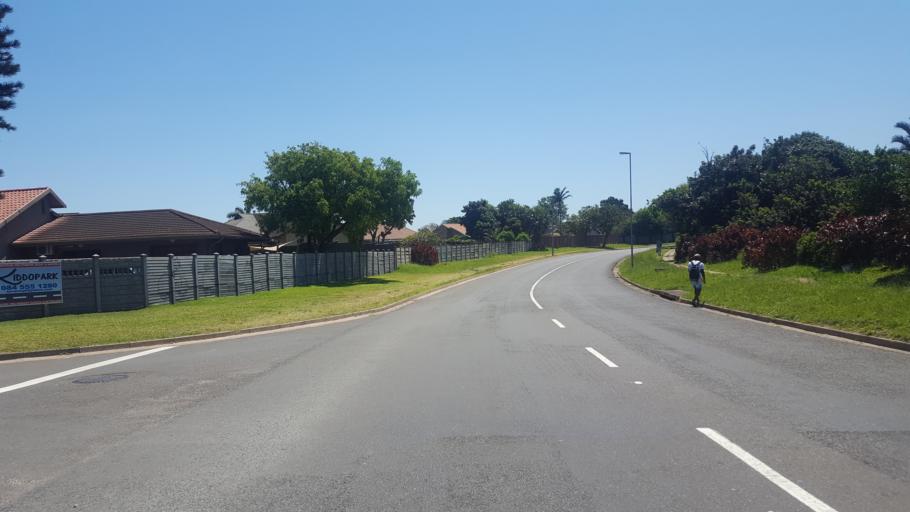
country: ZA
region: KwaZulu-Natal
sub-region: uThungulu District Municipality
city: Richards Bay
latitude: -28.7633
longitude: 32.0638
